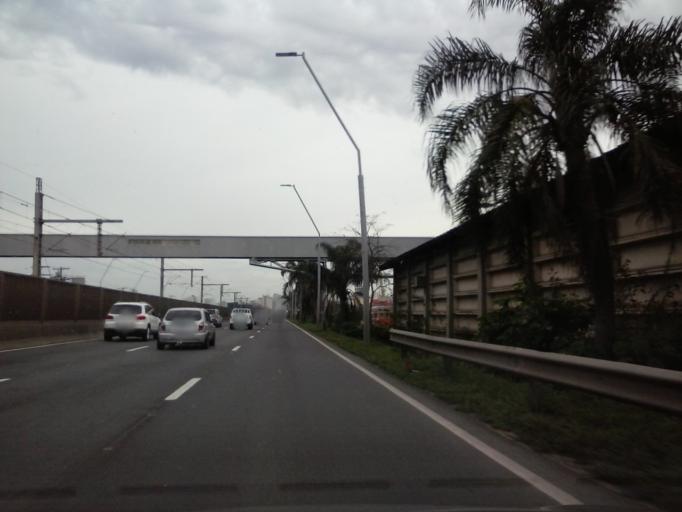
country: BR
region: Rio Grande do Sul
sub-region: Porto Alegre
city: Porto Alegre
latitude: -30.0087
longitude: -51.2108
